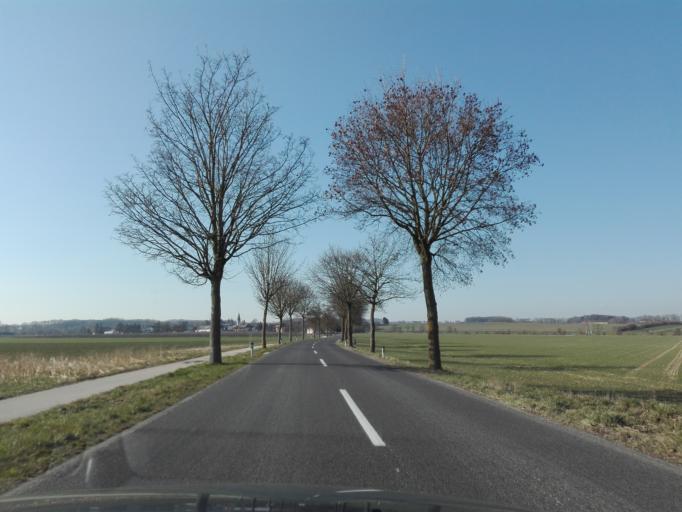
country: AT
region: Upper Austria
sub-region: Politischer Bezirk Linz-Land
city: Horsching
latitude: 48.2300
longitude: 14.1465
